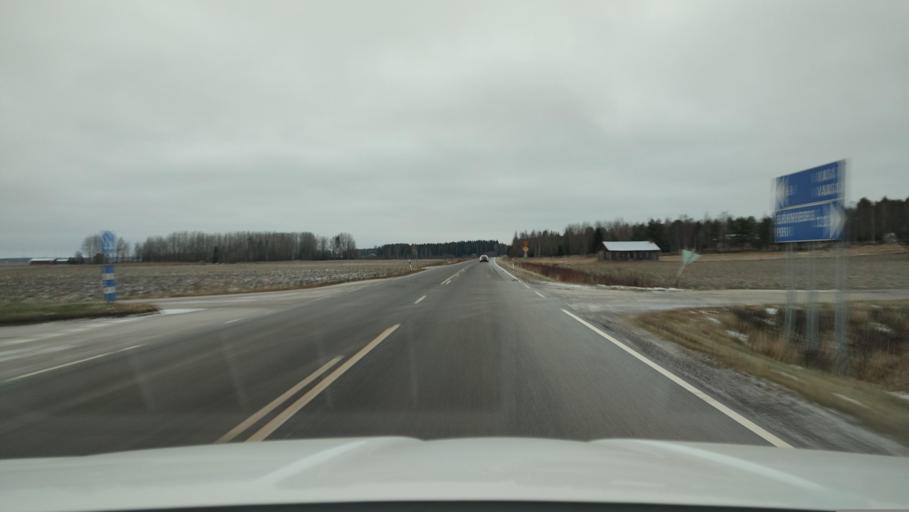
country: FI
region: Ostrobothnia
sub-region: Sydosterbotten
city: Naerpes
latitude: 62.5421
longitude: 21.4676
